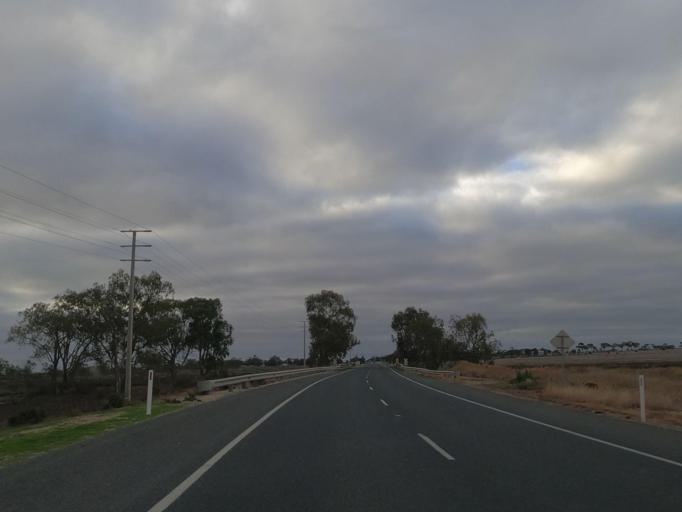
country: AU
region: Victoria
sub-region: Swan Hill
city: Swan Hill
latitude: -35.6199
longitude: 143.8034
